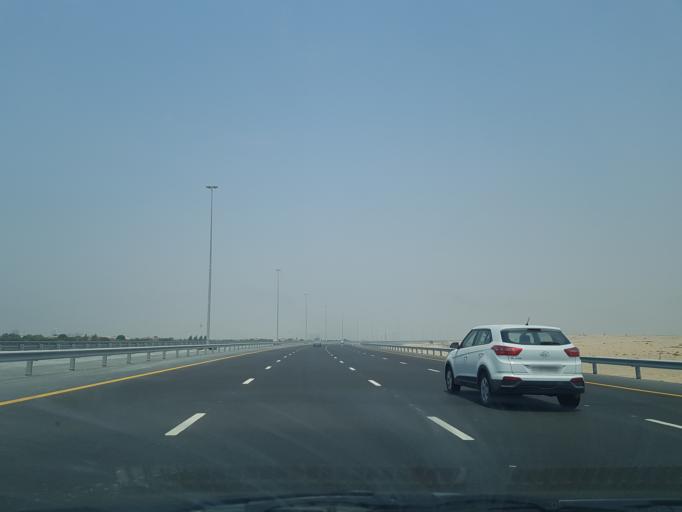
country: AE
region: Dubai
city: Dubai
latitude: 25.0091
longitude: 55.1990
